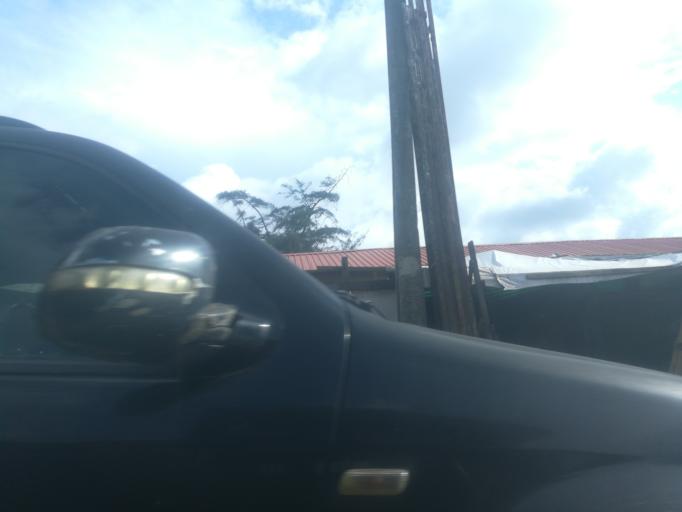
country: NG
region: Lagos
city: Somolu
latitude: 6.5463
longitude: 3.3764
